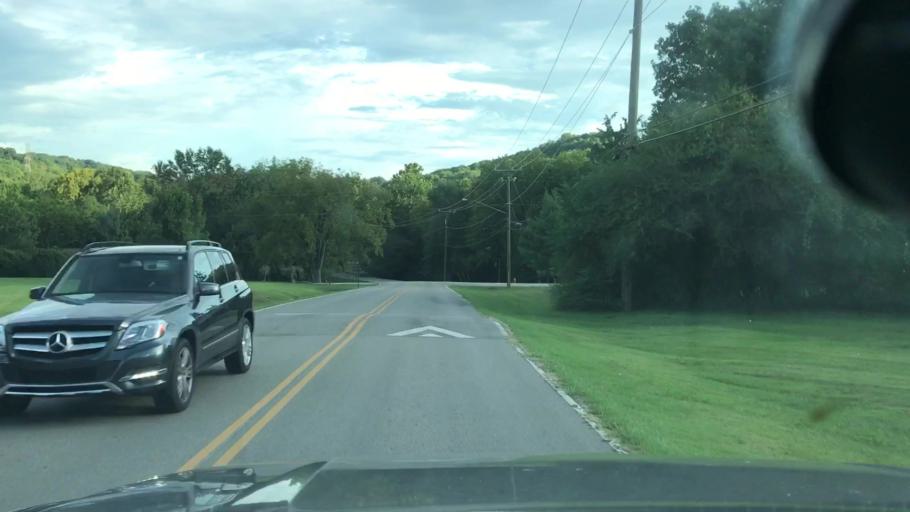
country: US
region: Tennessee
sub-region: Davidson County
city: Forest Hills
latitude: 36.0594
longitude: -86.8457
